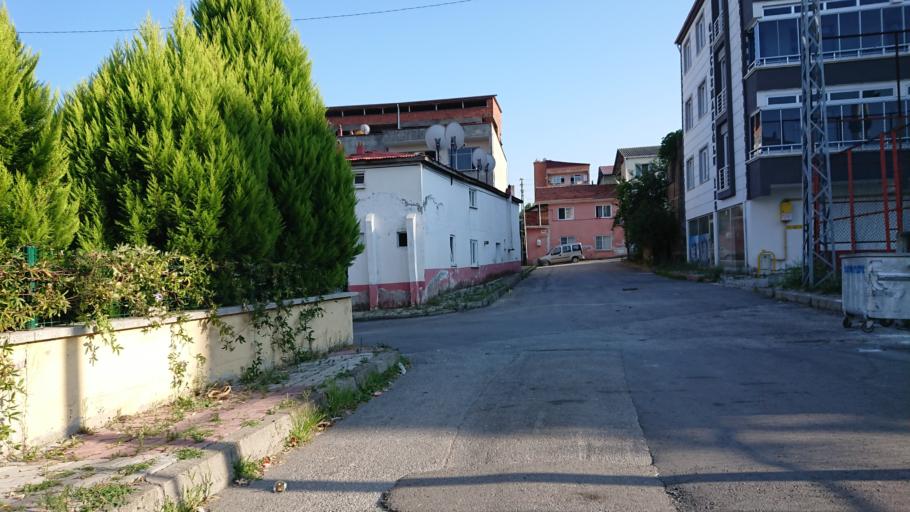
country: TR
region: Samsun
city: Samsun
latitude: 41.2987
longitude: 36.3208
